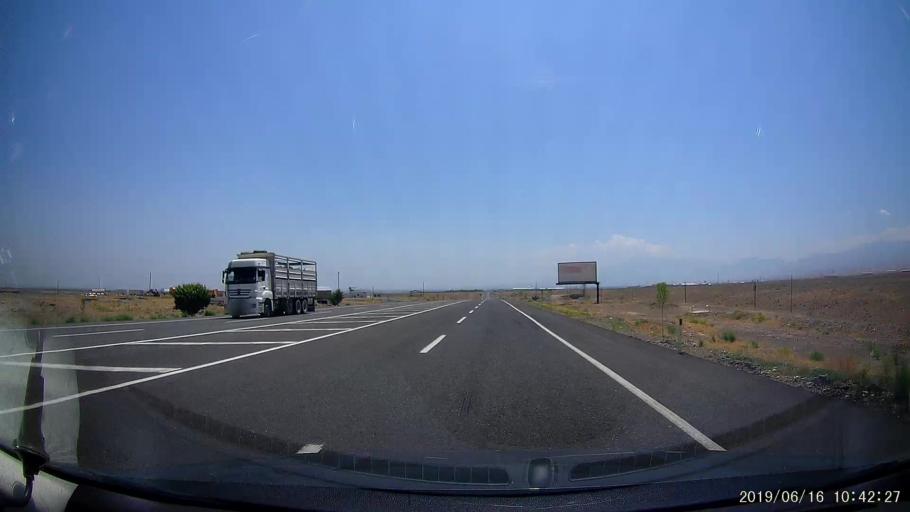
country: AM
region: Armavir
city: Shenavan
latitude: 40.0419
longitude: 43.8068
